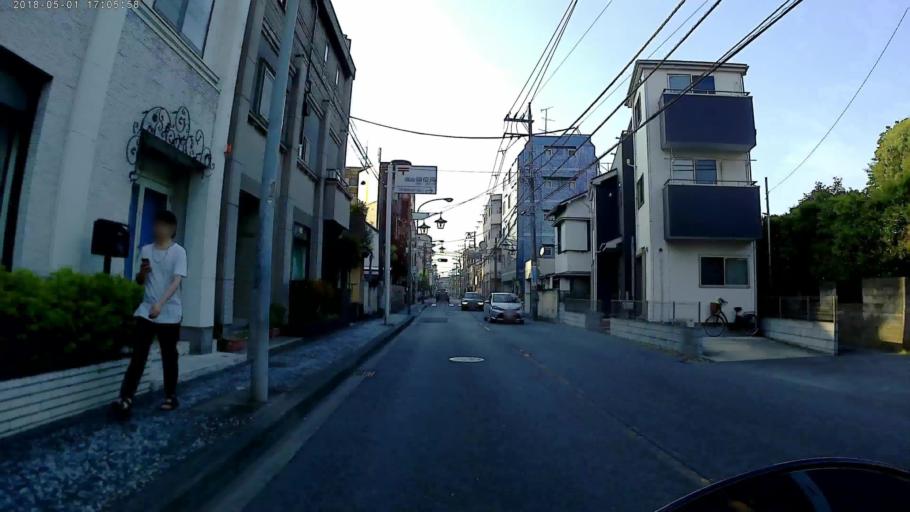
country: JP
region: Kanagawa
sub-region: Kawasaki-shi
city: Kawasaki
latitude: 35.5401
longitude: 139.6285
